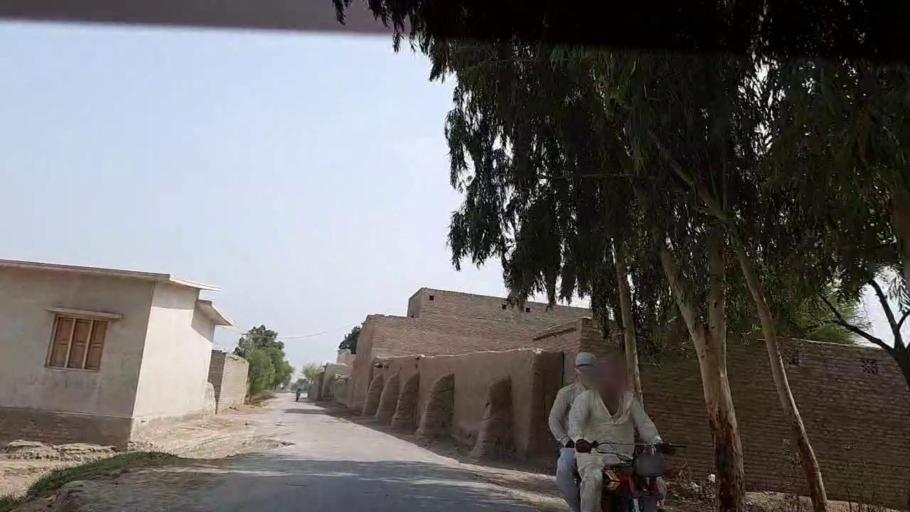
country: PK
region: Sindh
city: Khairpur Nathan Shah
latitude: 27.0611
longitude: 67.6861
